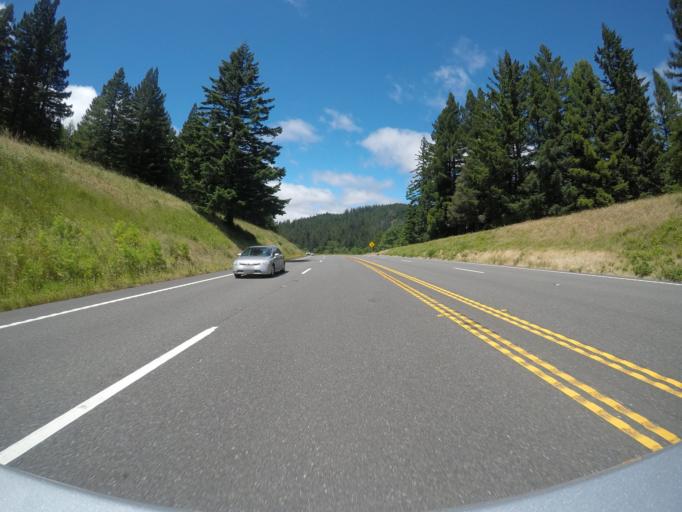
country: US
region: California
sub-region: Humboldt County
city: Redway
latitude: 40.2512
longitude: -123.8320
